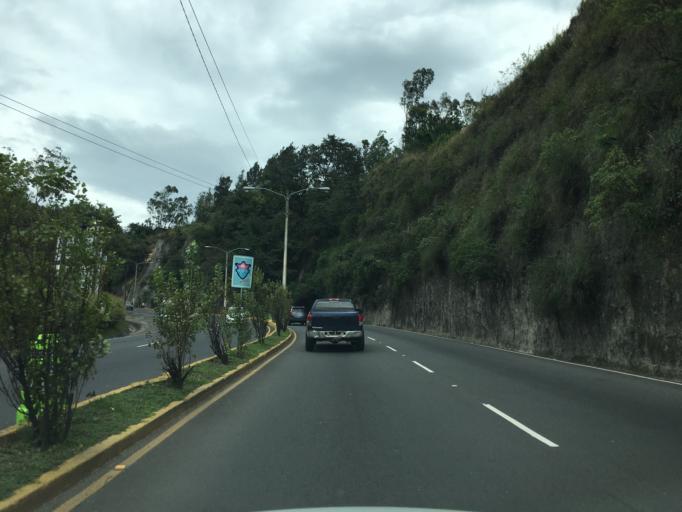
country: GT
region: Guatemala
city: Mixco
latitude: 14.5928
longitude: -90.5721
